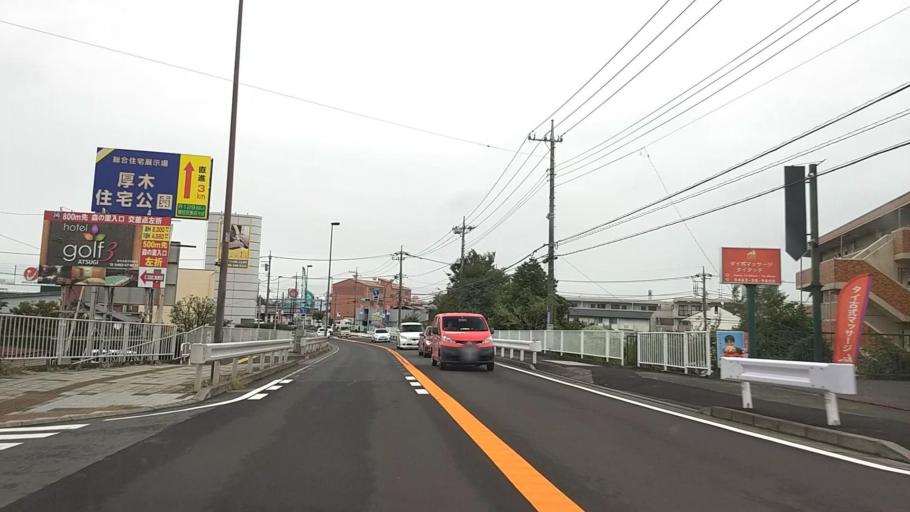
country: JP
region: Kanagawa
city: Atsugi
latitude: 35.4221
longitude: 139.3481
